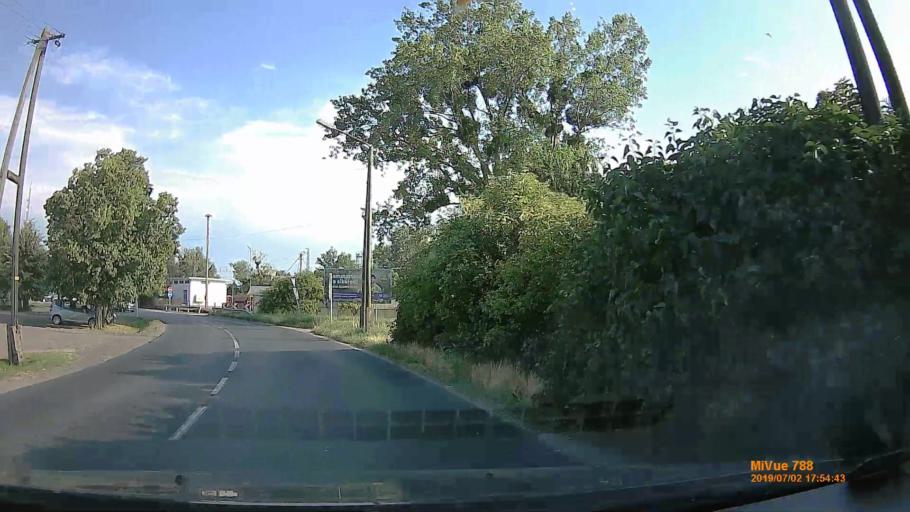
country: HU
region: Gyor-Moson-Sopron
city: Mosonmagyarovar
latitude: 47.8522
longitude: 17.2648
